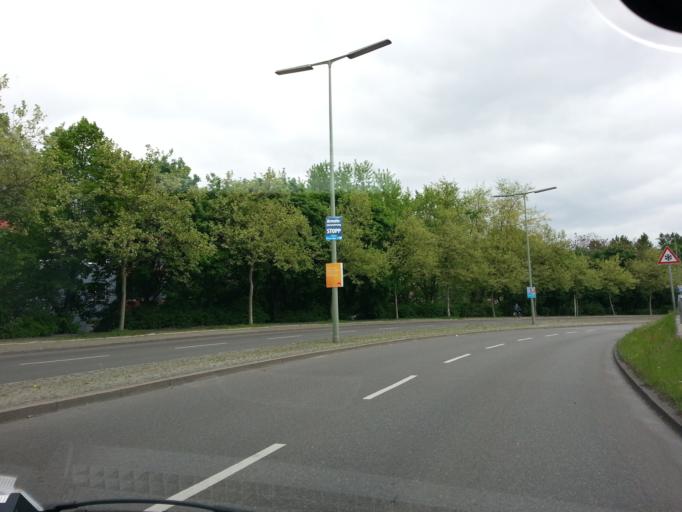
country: DE
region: Berlin
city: Charlottenburg-Nord
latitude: 52.5348
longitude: 13.2953
